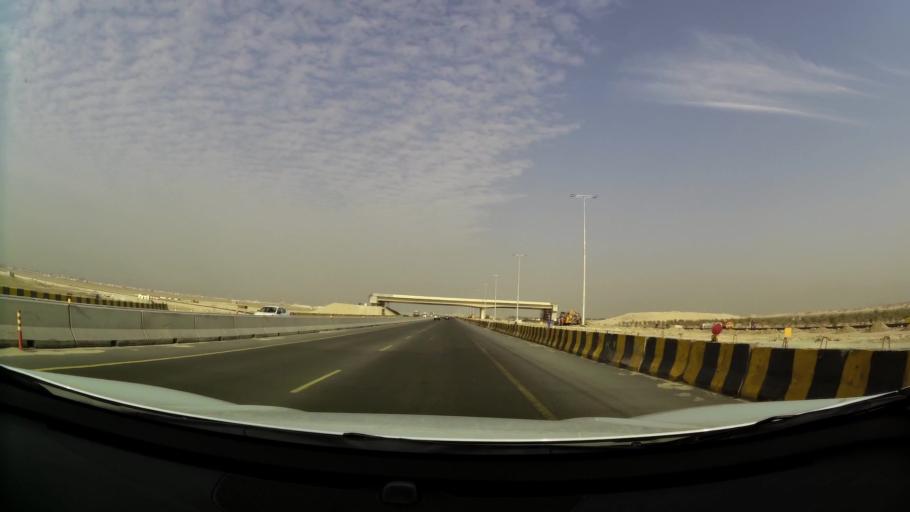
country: AE
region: Abu Dhabi
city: Abu Dhabi
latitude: 24.2774
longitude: 54.5214
